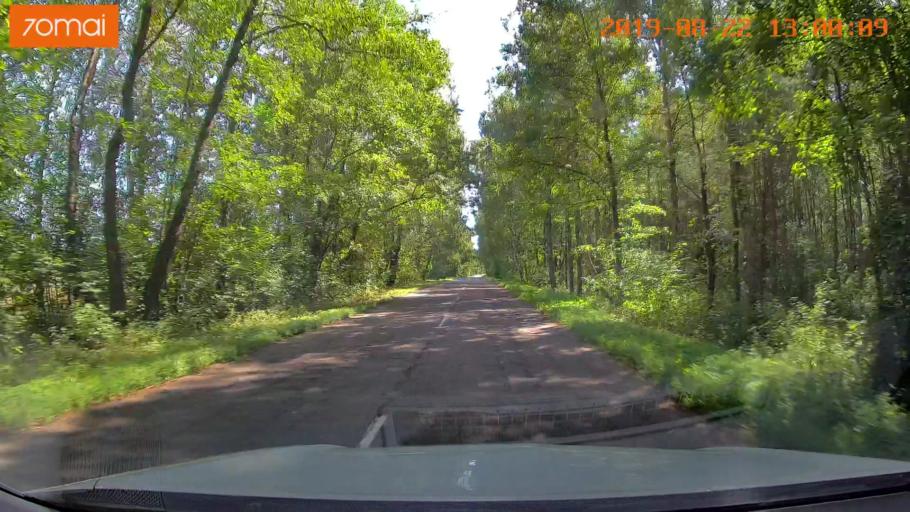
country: BY
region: Minsk
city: Prawdzinski
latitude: 53.4182
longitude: 27.8050
